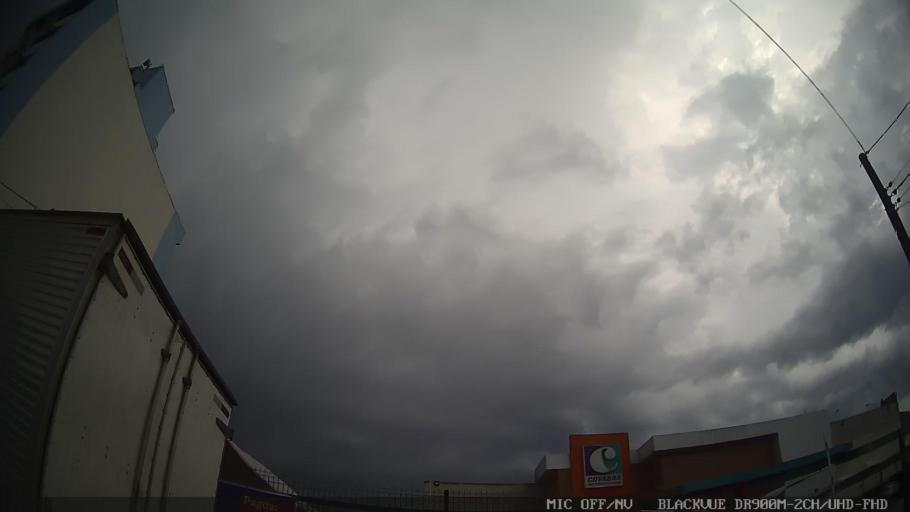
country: BR
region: Sao Paulo
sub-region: Itatiba
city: Itatiba
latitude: -23.0067
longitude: -46.8357
